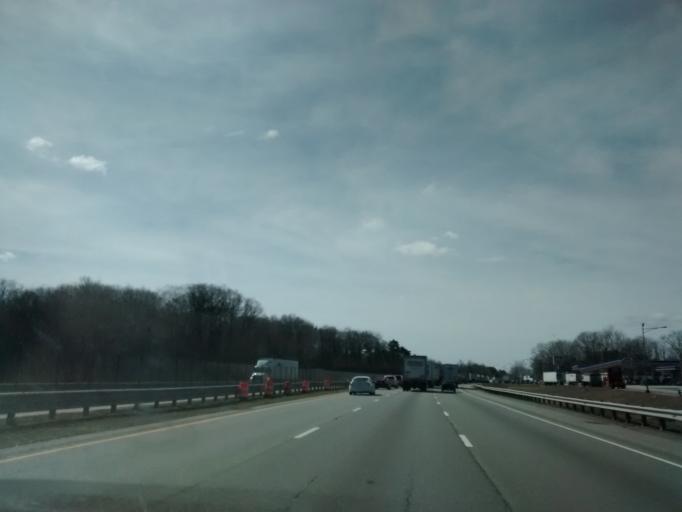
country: US
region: Massachusetts
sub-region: Worcester County
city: Charlton
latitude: 42.1566
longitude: -71.9619
